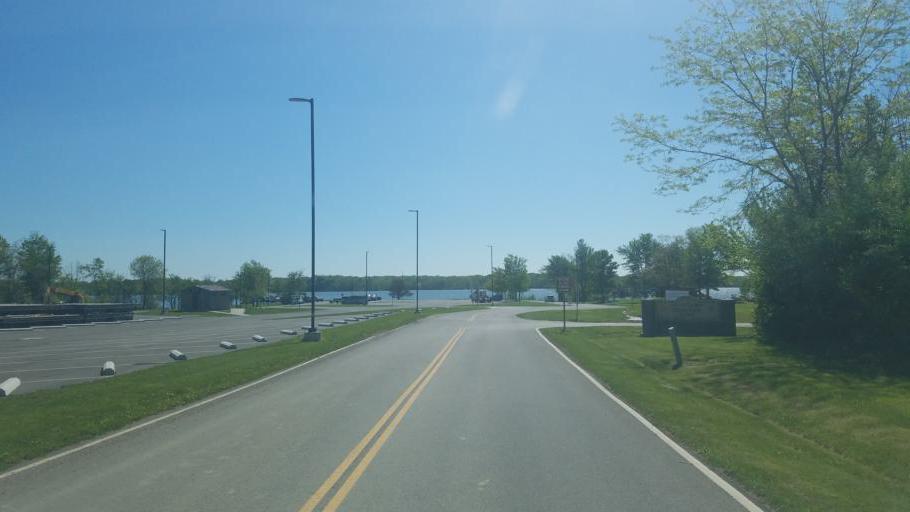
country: US
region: Ohio
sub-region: Delaware County
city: Lewis Center
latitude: 40.2123
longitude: -82.9749
